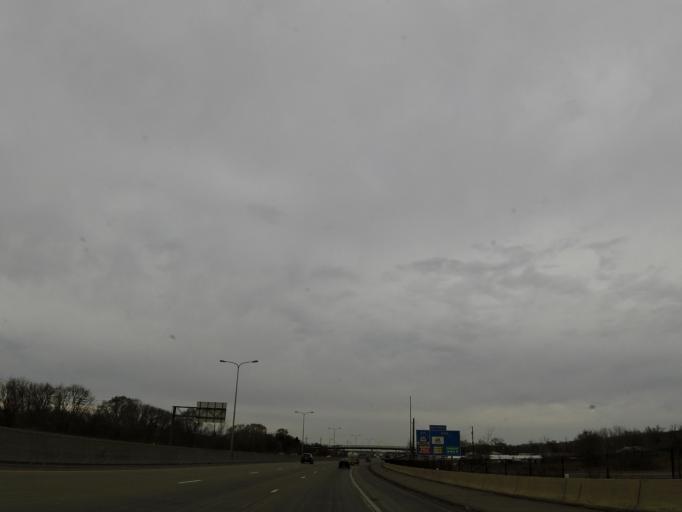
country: US
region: Minnesota
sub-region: Washington County
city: Newport
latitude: 44.8613
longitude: -92.9969
